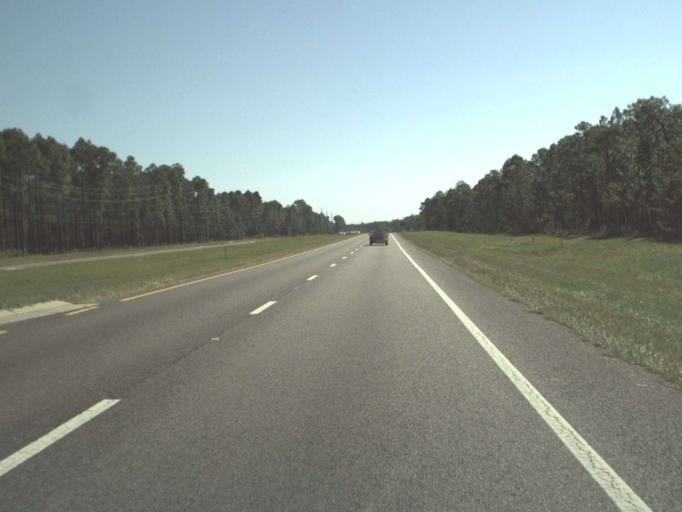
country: US
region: Florida
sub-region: Walton County
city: Seaside
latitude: 30.3614
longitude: -86.1645
